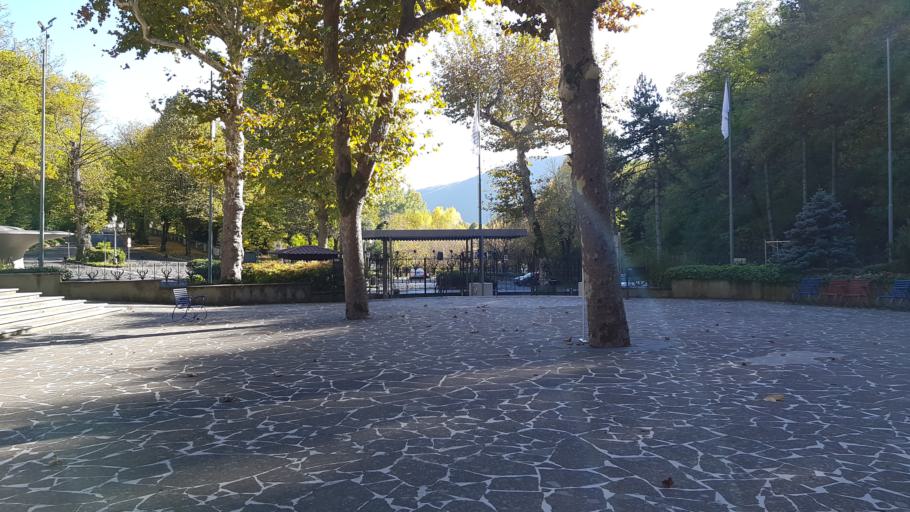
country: IT
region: Latium
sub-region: Provincia di Frosinone
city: Fiuggi
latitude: 41.7887
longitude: 13.2212
